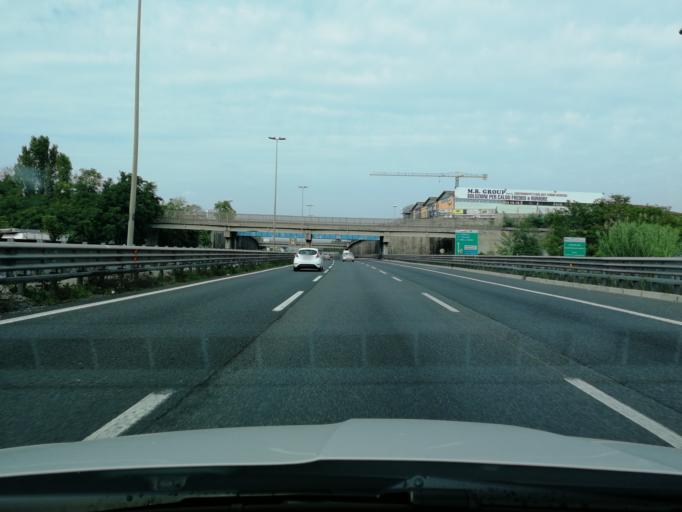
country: IT
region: Latium
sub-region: Citta metropolitana di Roma Capitale
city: Setteville
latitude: 41.8906
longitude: 12.6151
